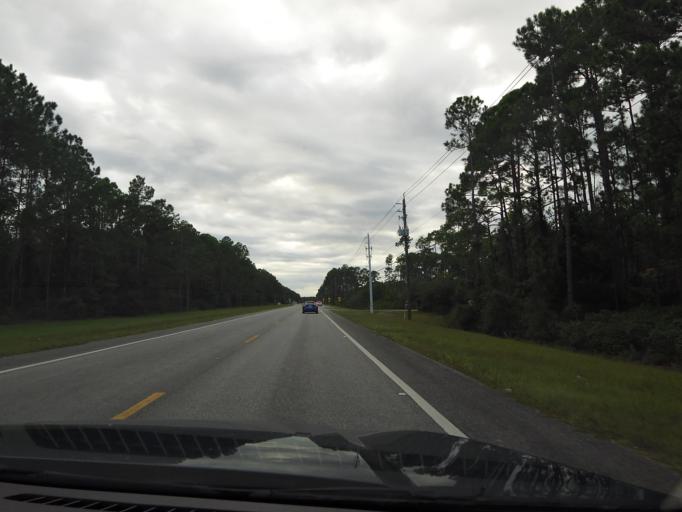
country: US
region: Florida
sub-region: Flagler County
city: Bunnell
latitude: 29.4973
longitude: -81.2502
